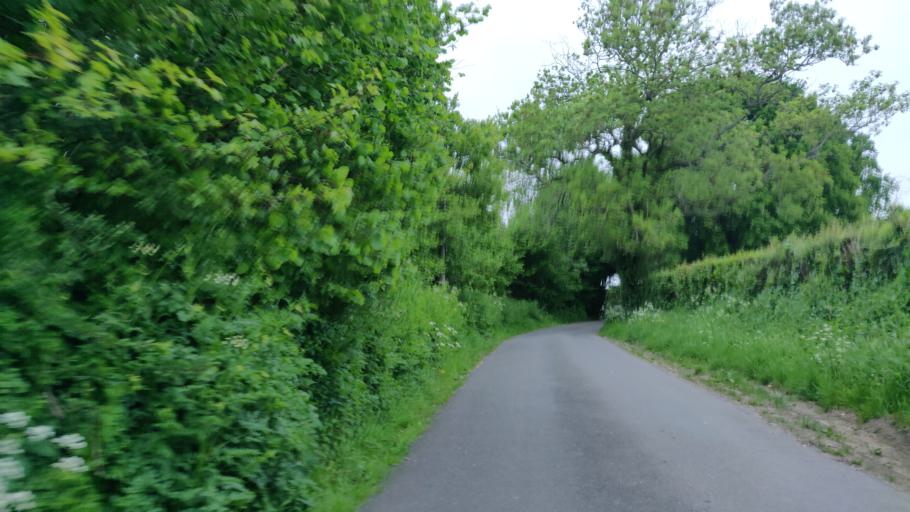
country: GB
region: England
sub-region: West Sussex
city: Southwater
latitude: 51.0298
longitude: -0.3337
